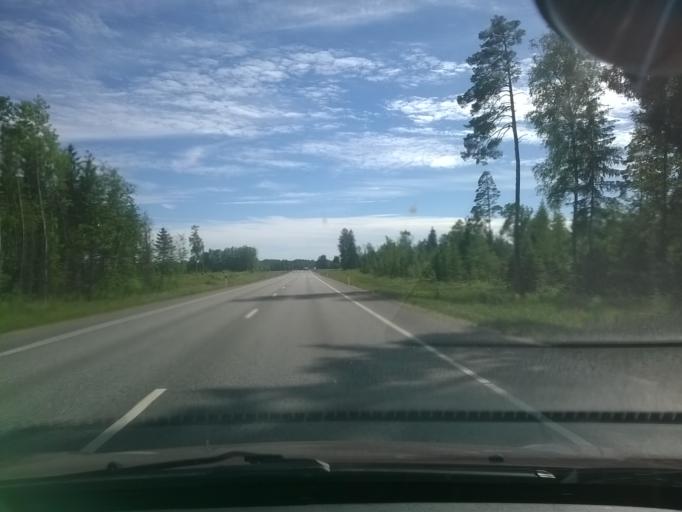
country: EE
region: Jaervamaa
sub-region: Paide linn
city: Paide
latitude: 58.9466
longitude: 25.6456
